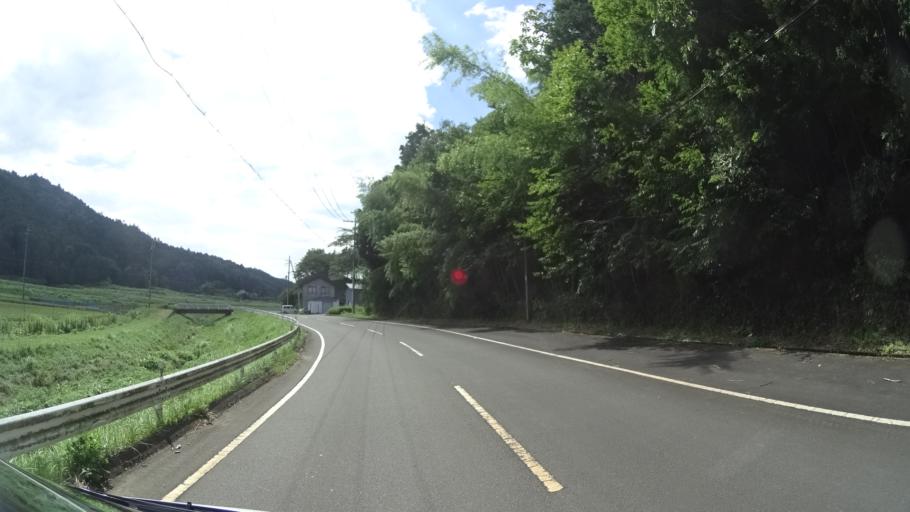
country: JP
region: Kyoto
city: Ayabe
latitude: 35.3696
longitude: 135.1868
